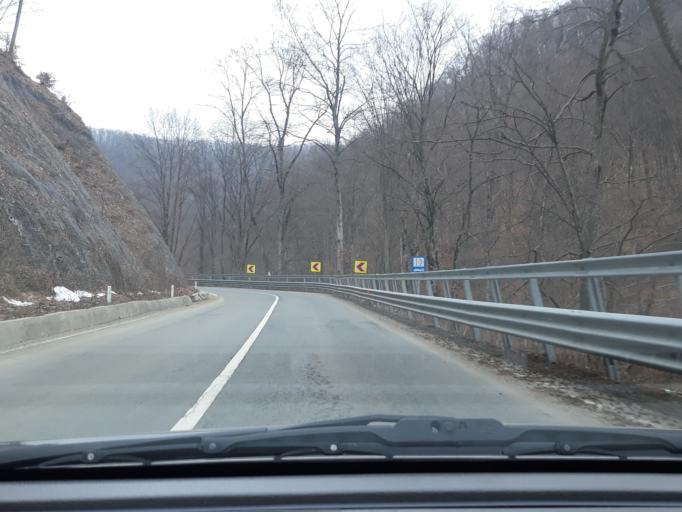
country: RO
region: Bihor
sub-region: Oras Alesd
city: Pestis
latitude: 47.1085
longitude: 22.4069
